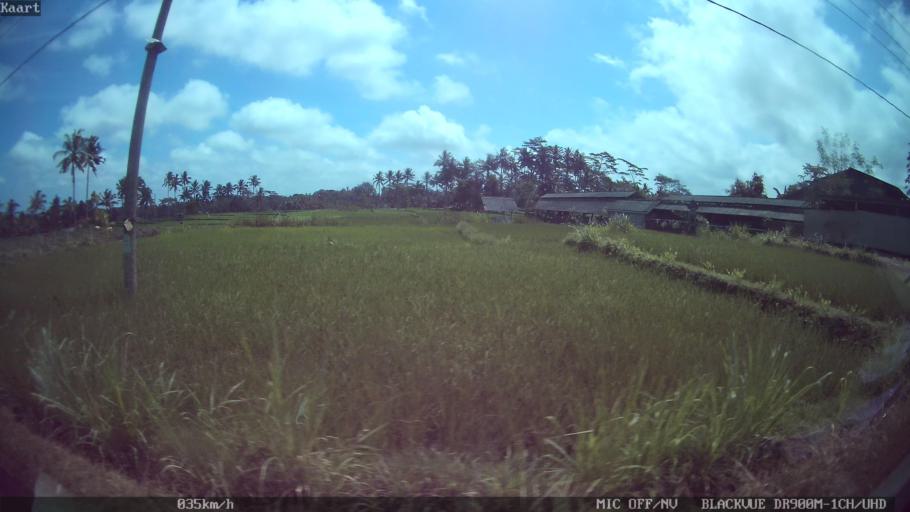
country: ID
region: Bali
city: Banjar Apuan Kaja
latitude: -8.4969
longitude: 115.3413
